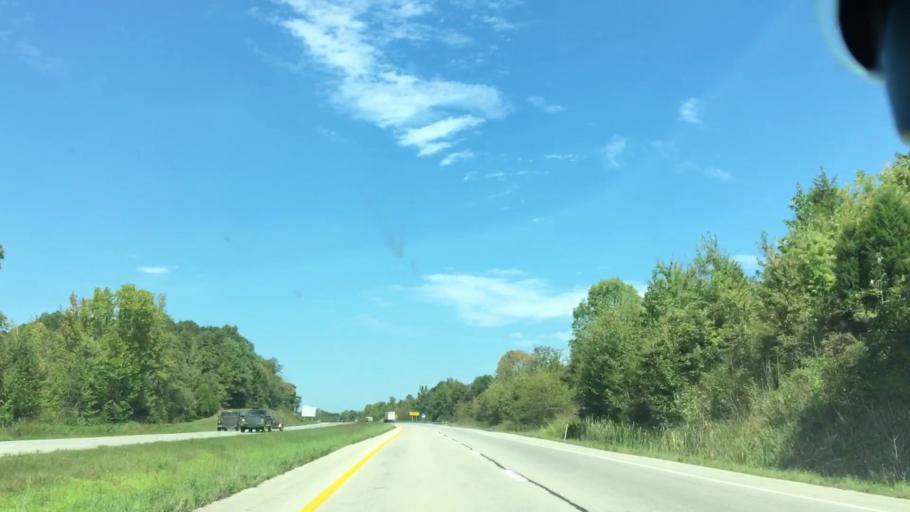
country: US
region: Kentucky
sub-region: Hopkins County
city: Nortonville
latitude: 37.1954
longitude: -87.4406
